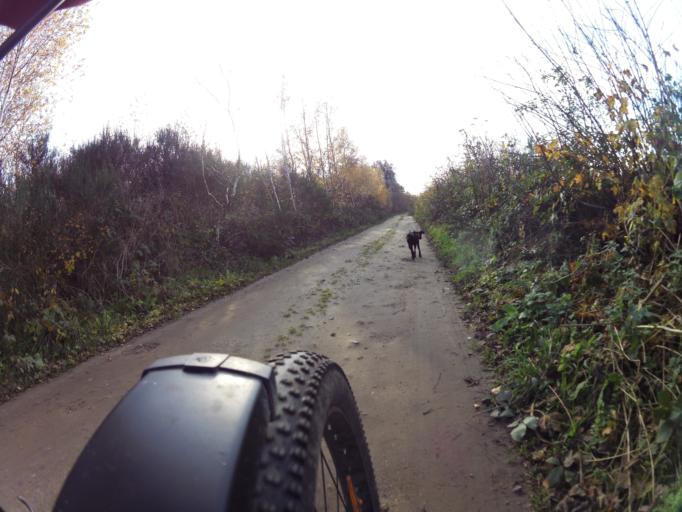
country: PL
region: Pomeranian Voivodeship
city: Strzelno
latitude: 54.7470
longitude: 18.2874
